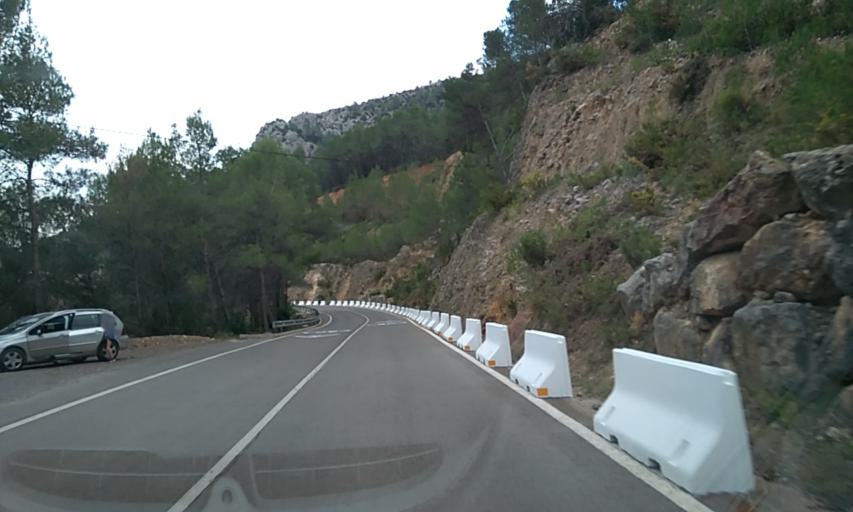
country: ES
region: Valencia
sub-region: Provincia de Castello
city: Montanejos
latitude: 40.0752
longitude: -0.5385
